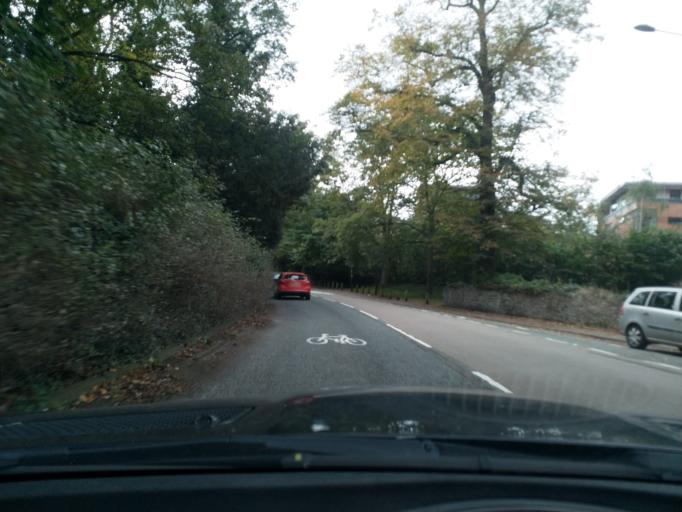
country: GB
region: England
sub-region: City and Borough of Birmingham
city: Birmingham
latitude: 52.4596
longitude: -1.9236
